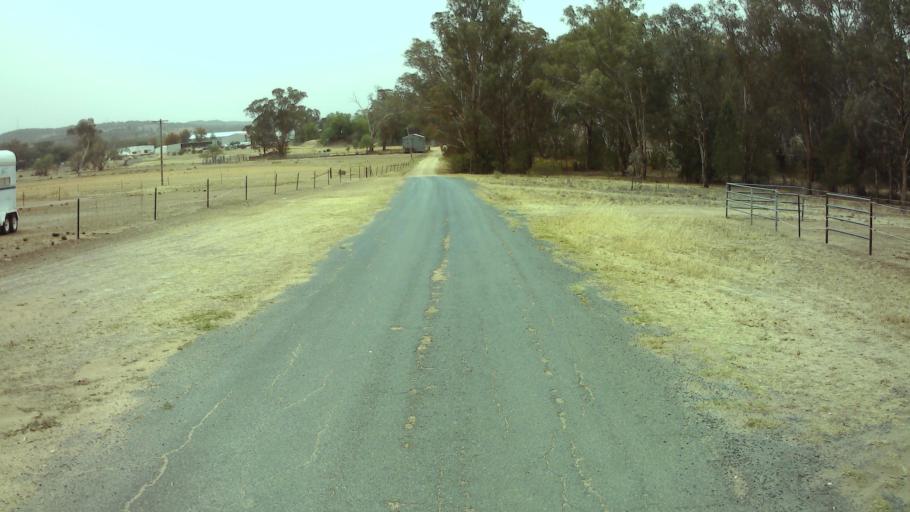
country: AU
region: New South Wales
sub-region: Weddin
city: Grenfell
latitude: -33.9058
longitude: 148.1541
